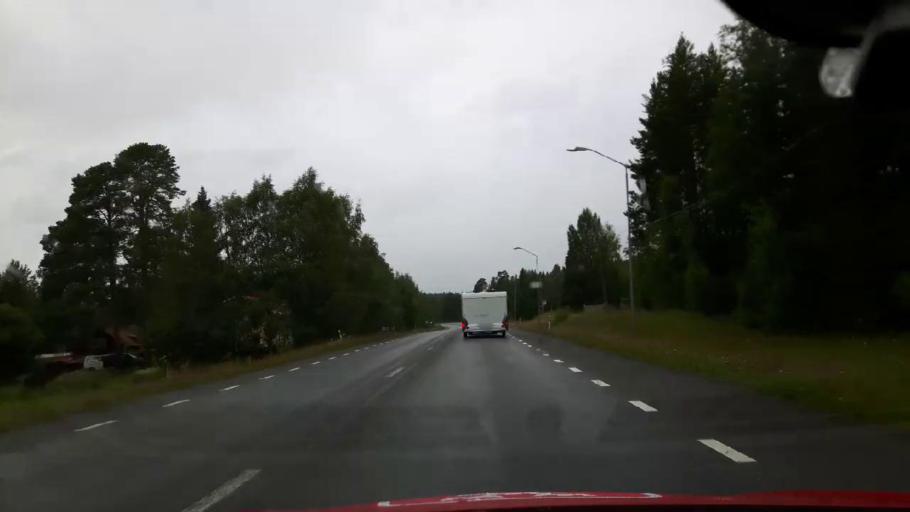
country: SE
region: Jaemtland
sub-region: Are Kommun
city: Jarpen
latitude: 63.3336
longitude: 13.5200
